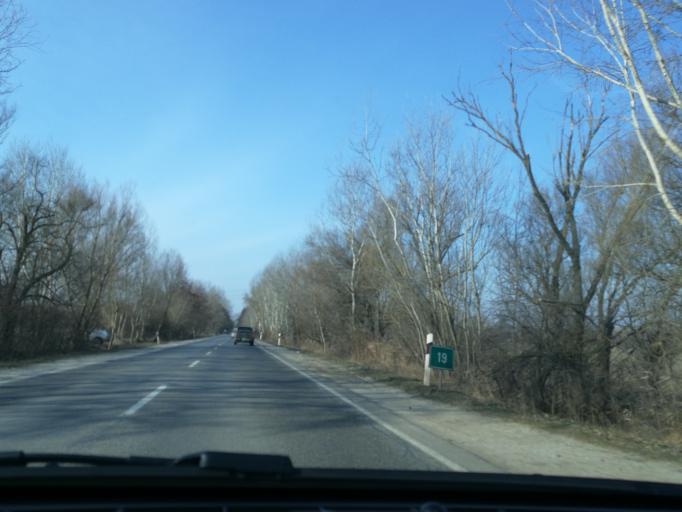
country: HU
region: Szabolcs-Szatmar-Bereg
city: Levelek
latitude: 47.9612
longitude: 21.9674
